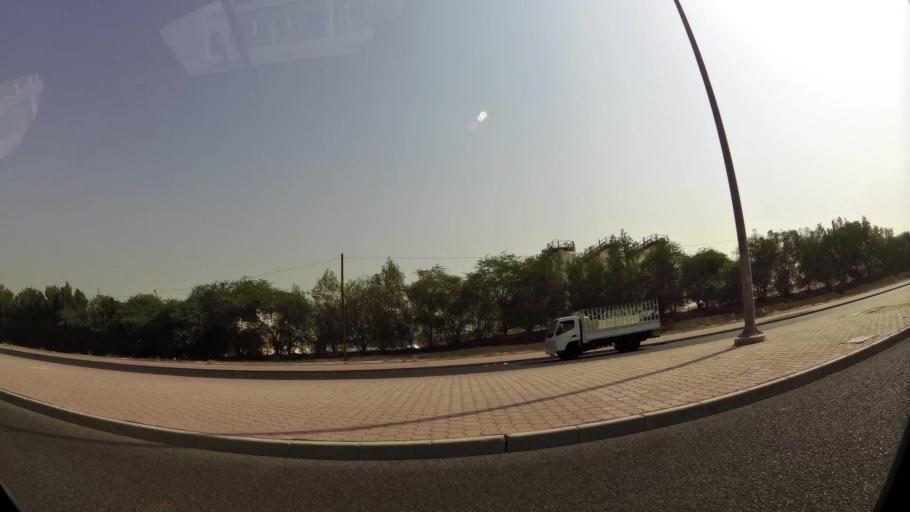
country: KW
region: Al Asimah
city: Ar Rabiyah
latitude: 29.2842
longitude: 47.9145
